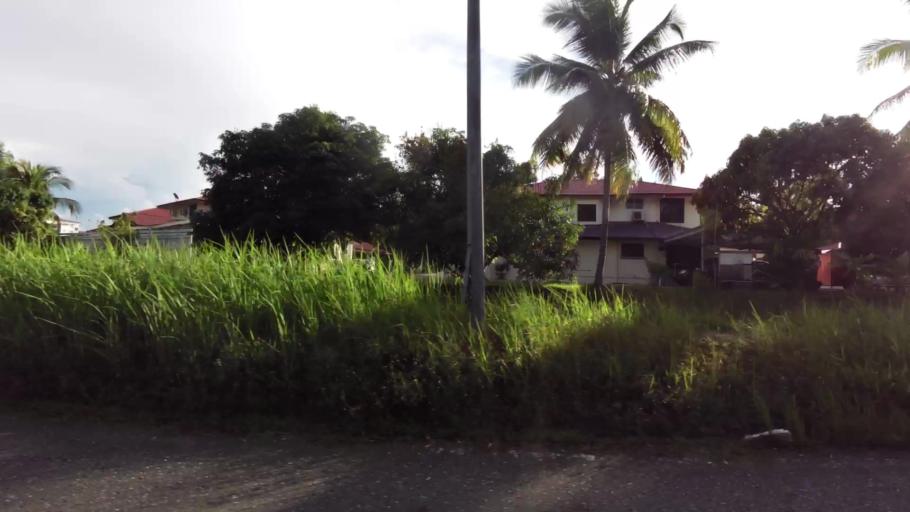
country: BN
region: Brunei and Muara
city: Bandar Seri Begawan
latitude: 4.9762
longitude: 114.9736
